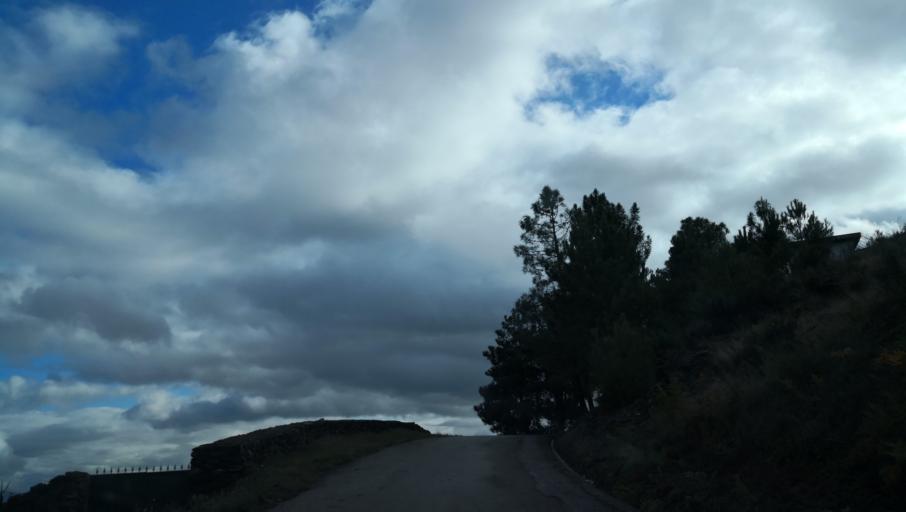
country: PT
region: Vila Real
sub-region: Sabrosa
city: Vilela
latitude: 41.1976
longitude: -7.5768
